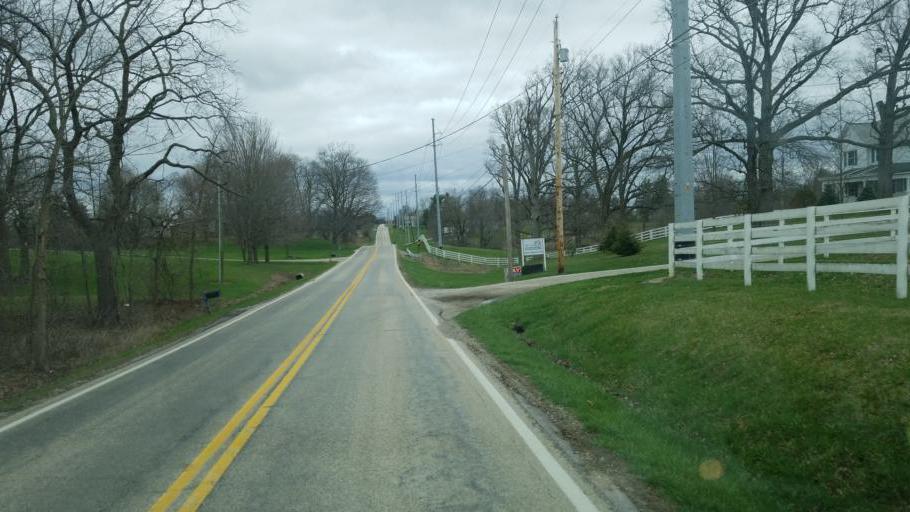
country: US
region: Ohio
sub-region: Delaware County
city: Delaware
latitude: 40.3451
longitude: -83.0990
